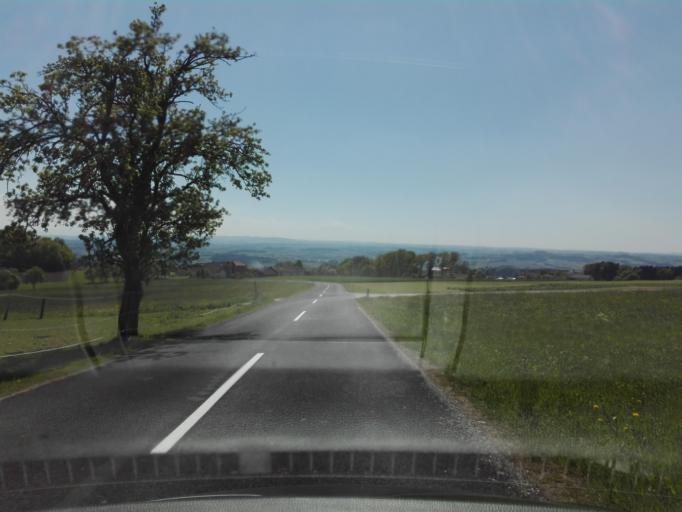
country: AT
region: Upper Austria
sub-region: Politischer Bezirk Rohrbach
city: Kleinzell im Muehlkreis
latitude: 48.3670
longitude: 13.9241
